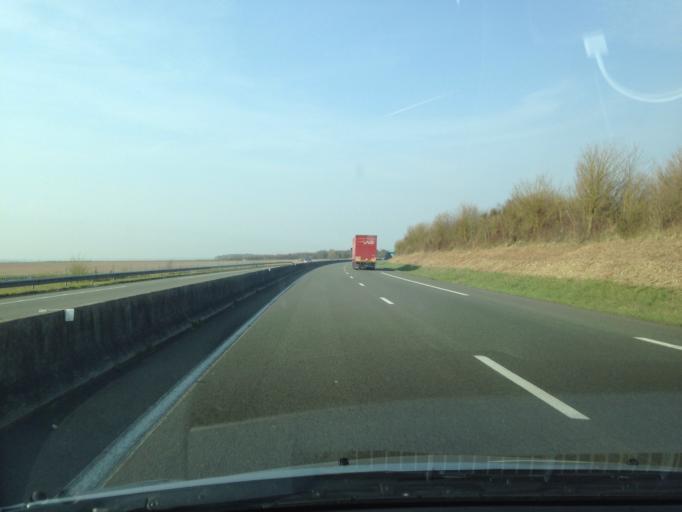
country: FR
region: Picardie
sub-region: Departement de la Somme
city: Sailly-Flibeaucourt
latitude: 50.1753
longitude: 1.7529
